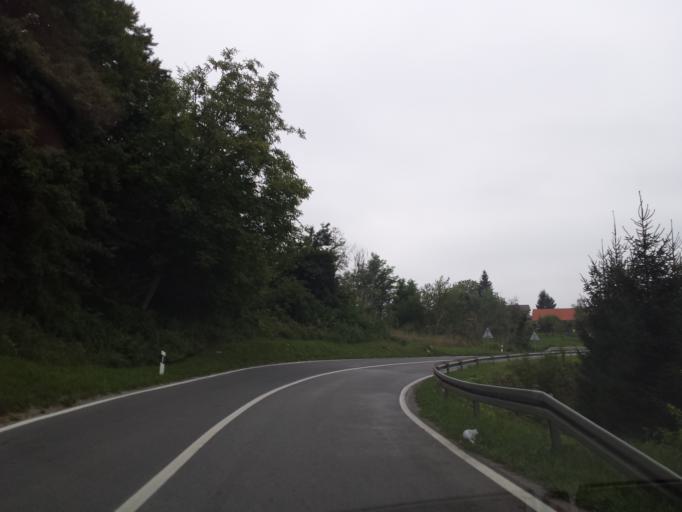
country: HR
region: Karlovacka
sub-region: Grad Karlovac
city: Karlovac
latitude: 45.4193
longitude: 15.4610
